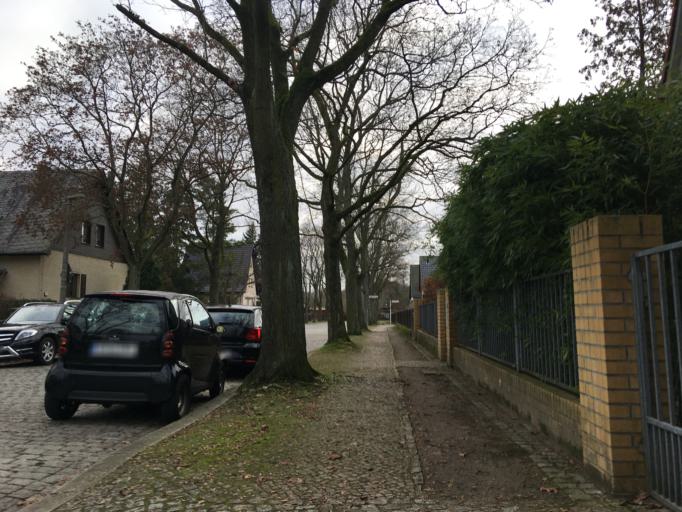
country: DE
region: Berlin
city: Niederschonhausen
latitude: 52.5805
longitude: 13.3891
